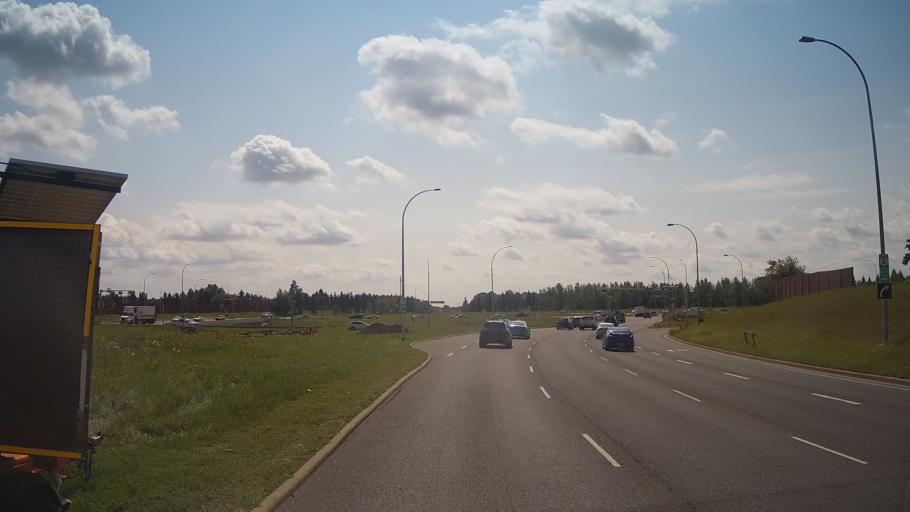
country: CA
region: Alberta
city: St. Albert
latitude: 53.5140
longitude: -113.6154
